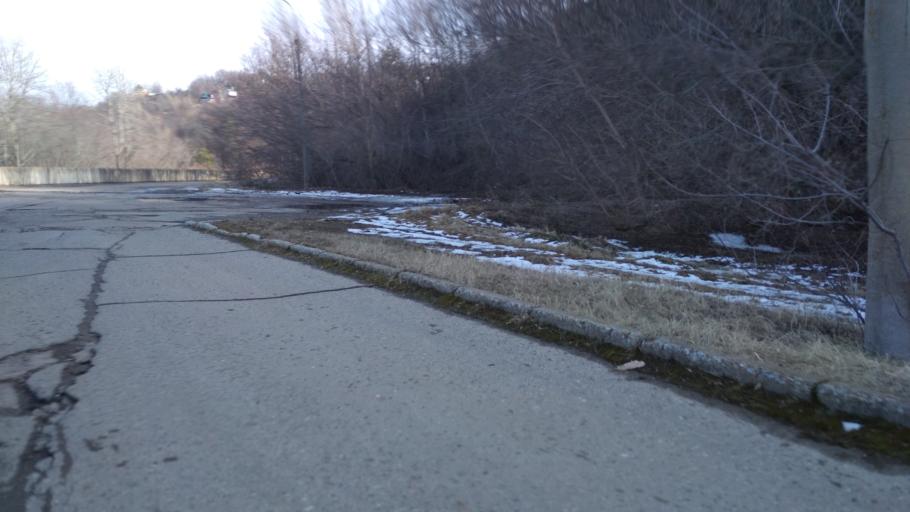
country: RU
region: Chuvashia
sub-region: Cheboksarskiy Rayon
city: Cheboksary
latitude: 56.1486
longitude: 47.2923
